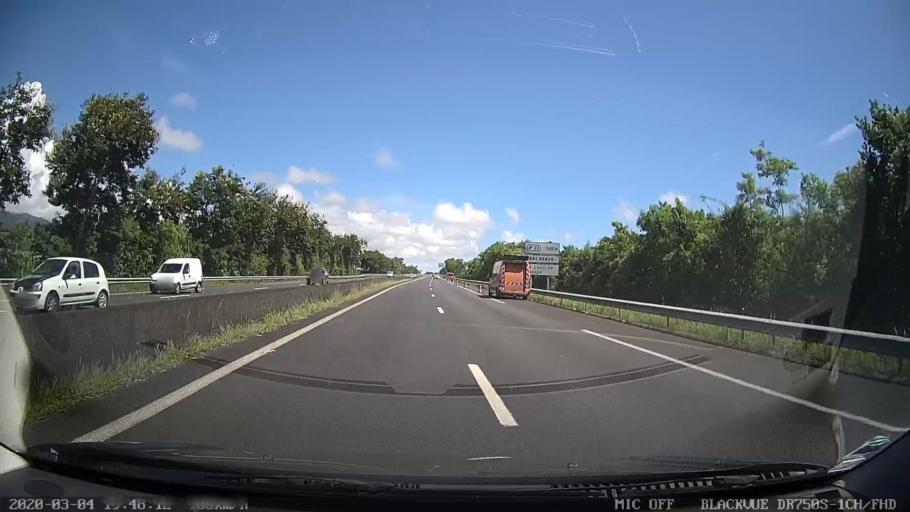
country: RE
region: Reunion
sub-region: Reunion
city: Bras-Panon
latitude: -21.0049
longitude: 55.6776
